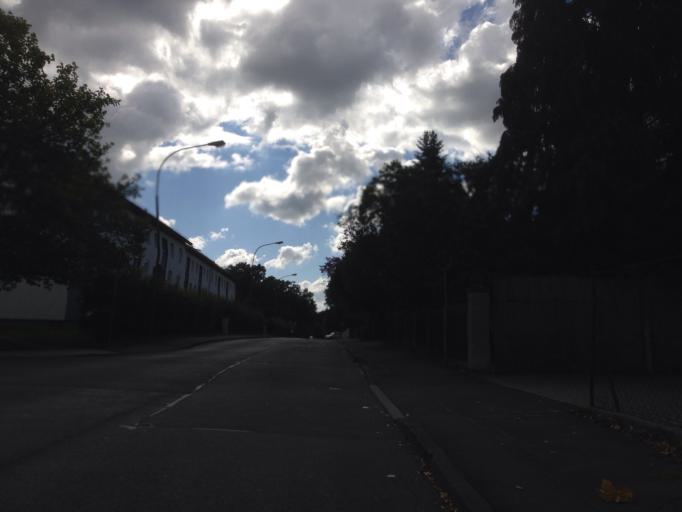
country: DE
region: Hesse
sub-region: Regierungsbezirk Giessen
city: Giessen
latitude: 50.5887
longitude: 8.7134
